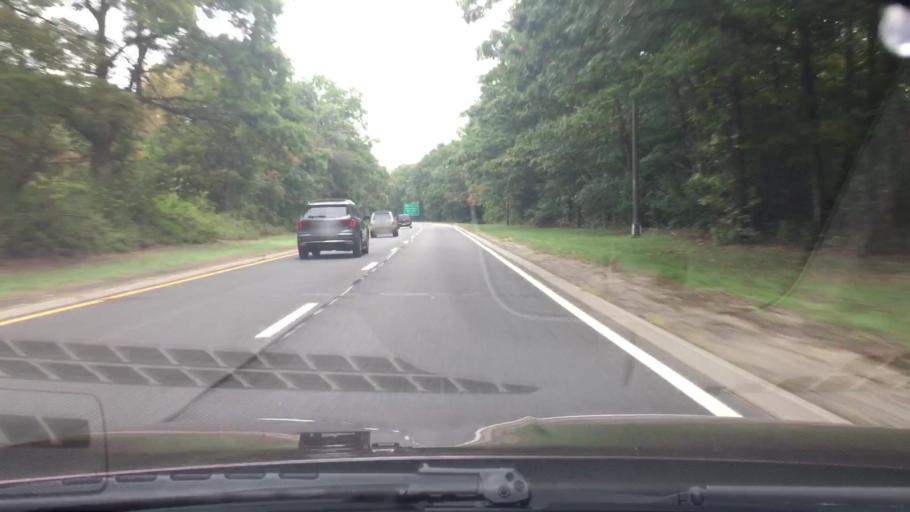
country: US
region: New York
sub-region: Suffolk County
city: South Huntington
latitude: 40.8013
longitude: -73.3890
